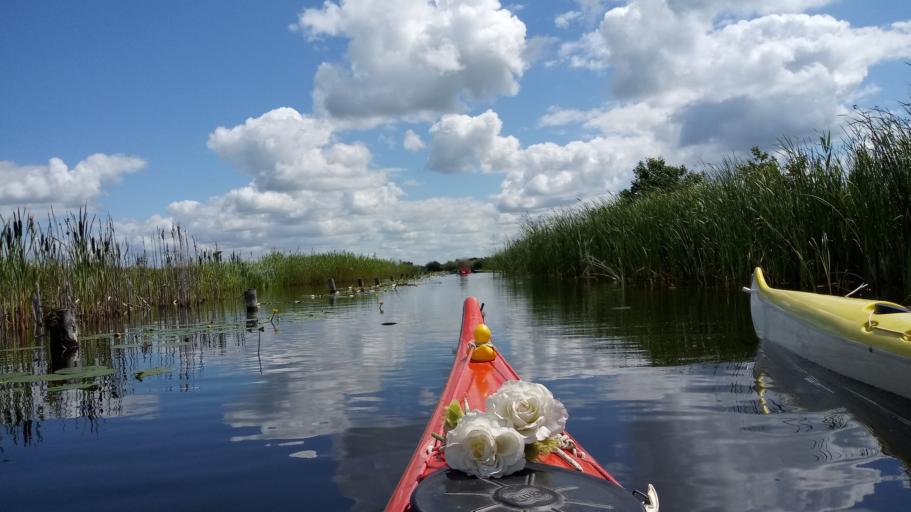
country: NL
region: Overijssel
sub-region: Gemeente Steenwijkerland
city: Giethoorn
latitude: 52.7074
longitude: 6.0827
